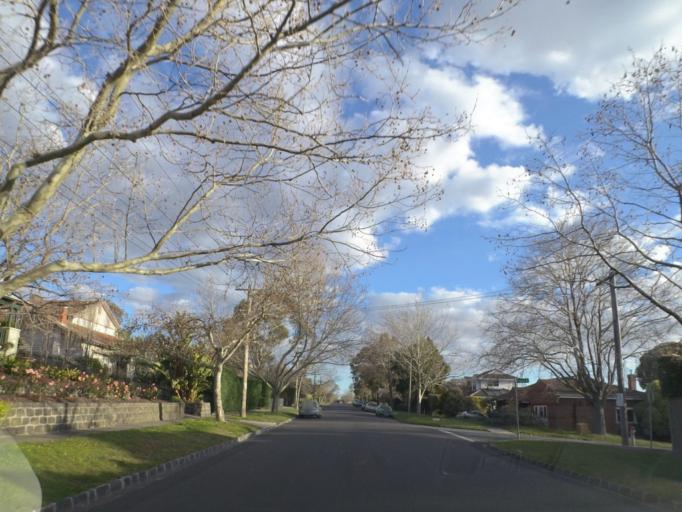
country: AU
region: Victoria
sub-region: Whitehorse
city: Surrey Hills
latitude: -37.8325
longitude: 145.0961
